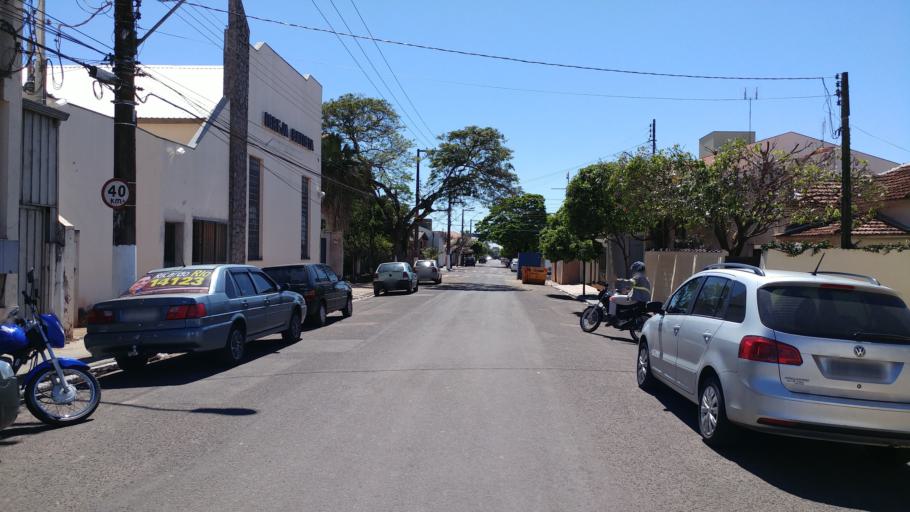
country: BR
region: Sao Paulo
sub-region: Paraguacu Paulista
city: Paraguacu Paulista
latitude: -22.4134
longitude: -50.5769
